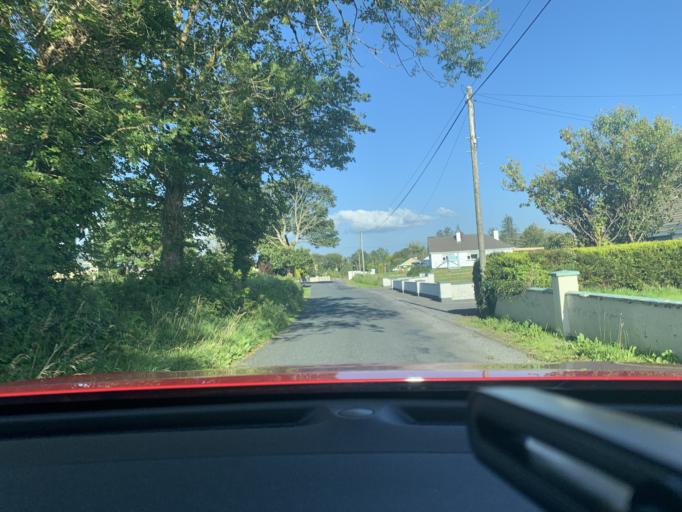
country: IE
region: Connaught
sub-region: Sligo
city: Strandhill
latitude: 54.1657
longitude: -8.6269
